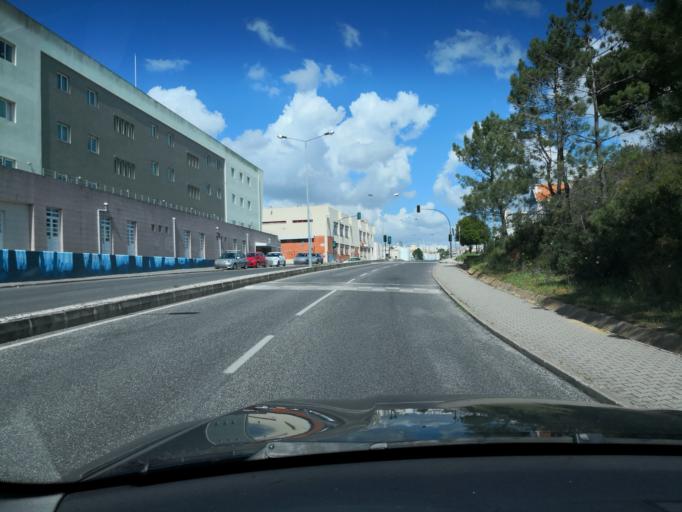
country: PT
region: Setubal
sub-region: Setubal
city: Setubal
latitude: 38.5228
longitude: -8.8613
